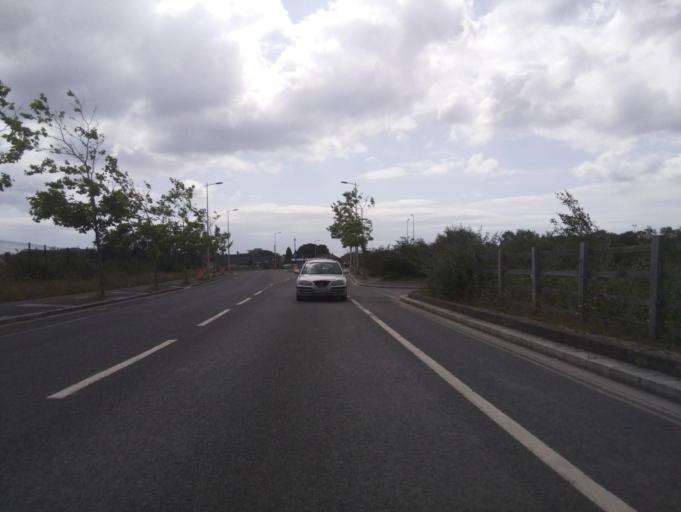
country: GB
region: England
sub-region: Poole
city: Poole
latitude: 50.7159
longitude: -1.9984
